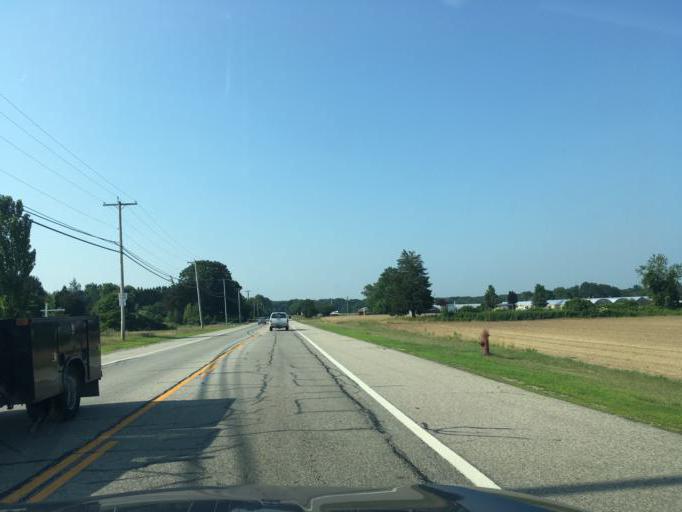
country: US
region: Rhode Island
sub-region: Washington County
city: Exeter
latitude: 41.5677
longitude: -71.5172
